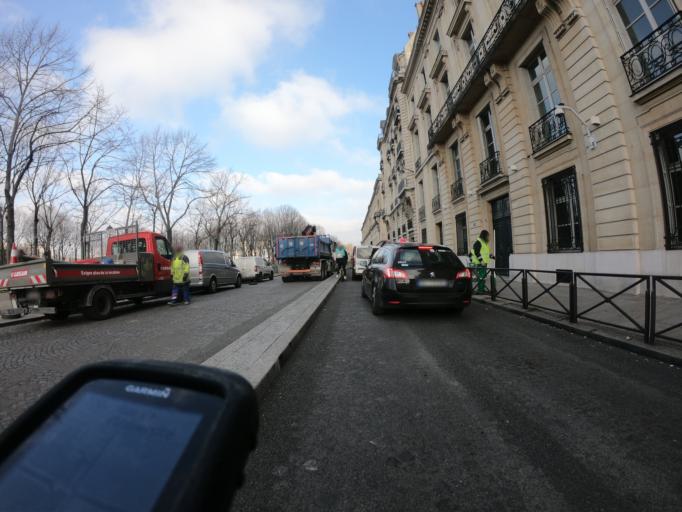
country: FR
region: Ile-de-France
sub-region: Paris
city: Paris
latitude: 48.8605
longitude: 2.3149
